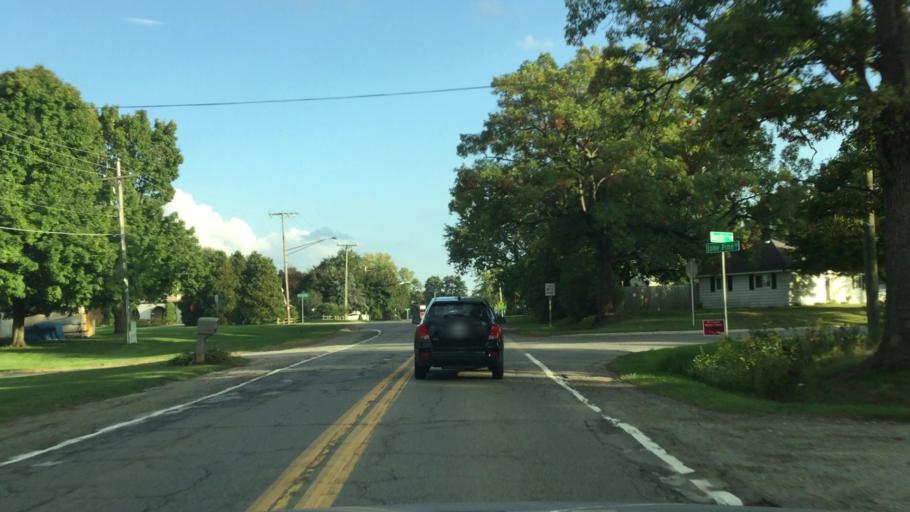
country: US
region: Michigan
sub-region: Oakland County
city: Waterford
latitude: 42.6391
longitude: -83.4710
